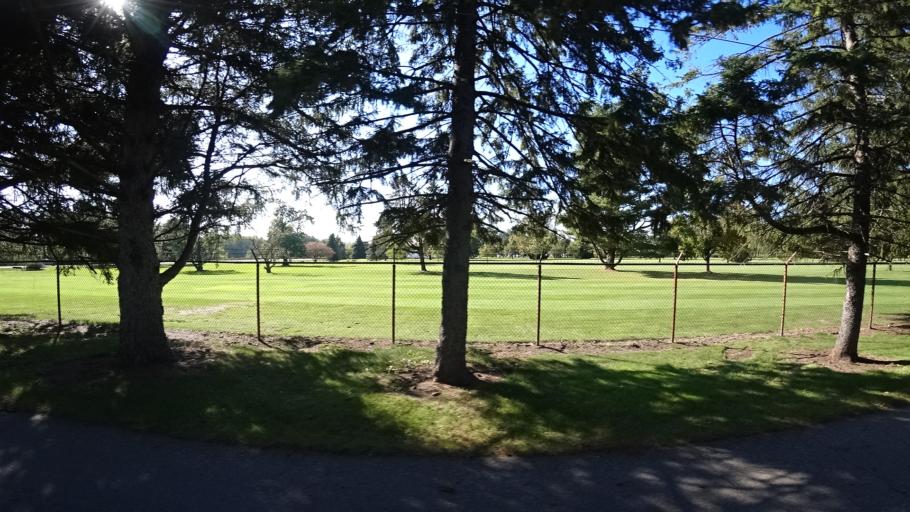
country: US
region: Indiana
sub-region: LaPorte County
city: Trail Creek
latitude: 41.7033
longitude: -86.8430
